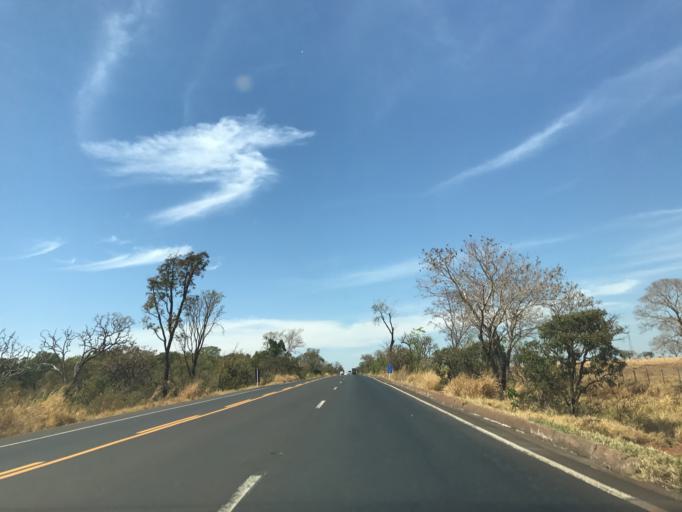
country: BR
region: Minas Gerais
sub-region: Monte Alegre De Minas
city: Monte Alegre de Minas
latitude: -19.0663
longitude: -49.0061
